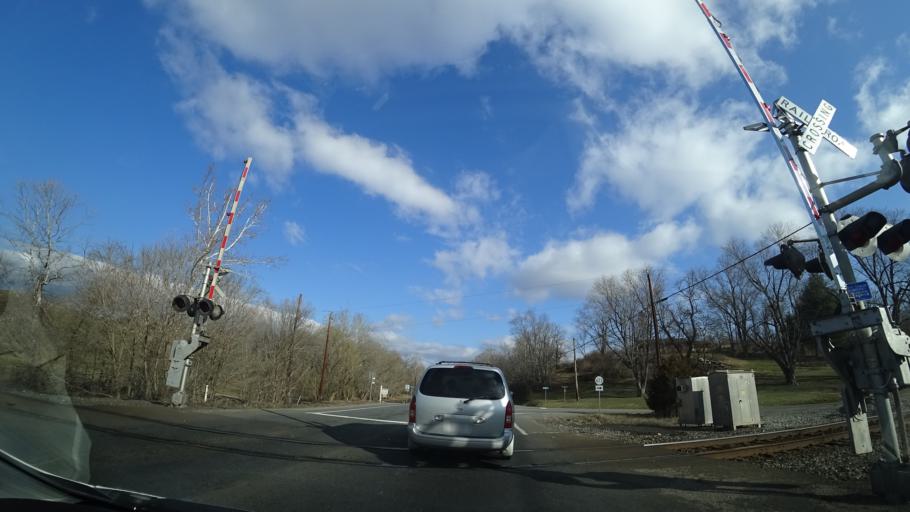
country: US
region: Virginia
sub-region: Fauquier County
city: Marshall
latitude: 38.9146
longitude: -77.9220
